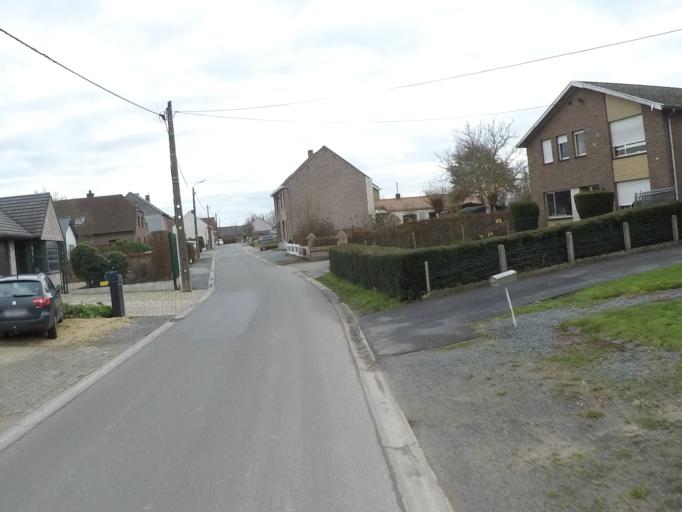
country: BE
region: Flanders
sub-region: Provincie Vlaams-Brabant
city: Merchtem
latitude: 50.9878
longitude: 4.2307
